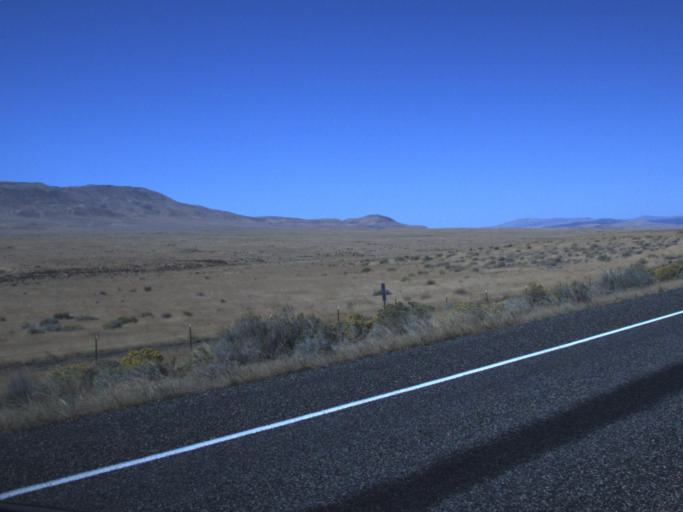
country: US
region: Washington
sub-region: Benton County
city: West Richland
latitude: 46.4180
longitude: -119.4621
